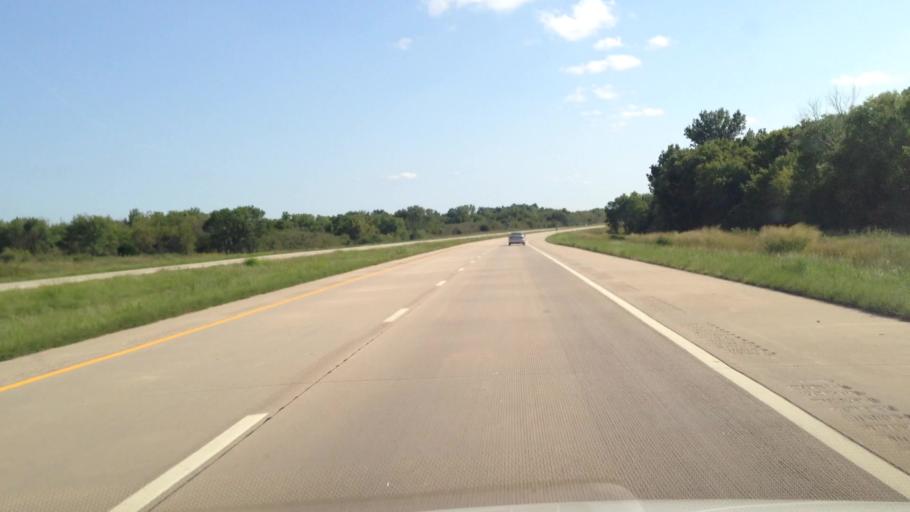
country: US
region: Kansas
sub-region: Bourbon County
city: Fort Scott
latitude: 37.9087
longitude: -94.7035
